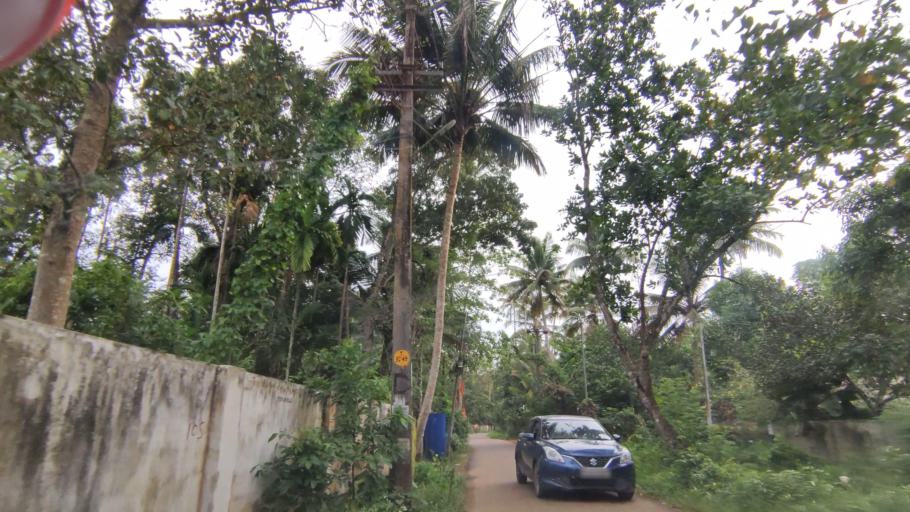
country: IN
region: Kerala
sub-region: Alappuzha
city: Shertallai
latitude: 9.6683
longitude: 76.3674
